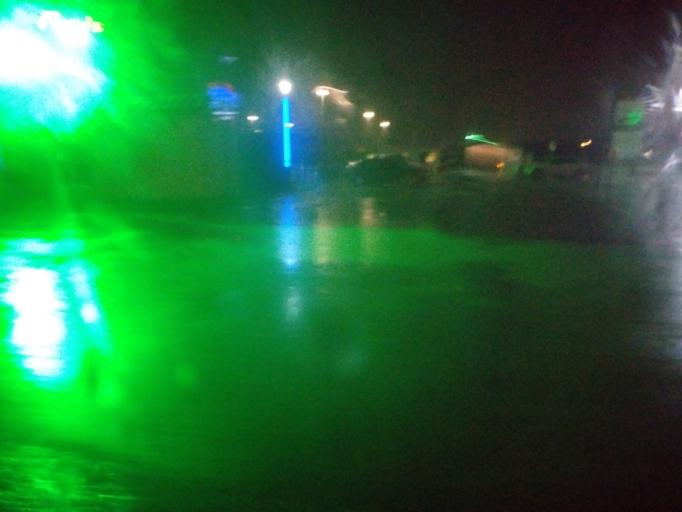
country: TR
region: Ankara
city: Ankara
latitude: 39.9687
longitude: 32.8234
